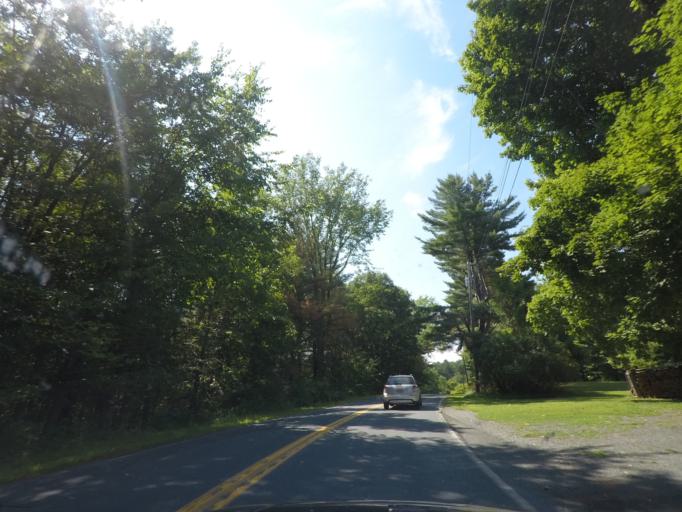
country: US
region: New York
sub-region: Rensselaer County
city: Averill Park
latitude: 42.5814
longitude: -73.5687
